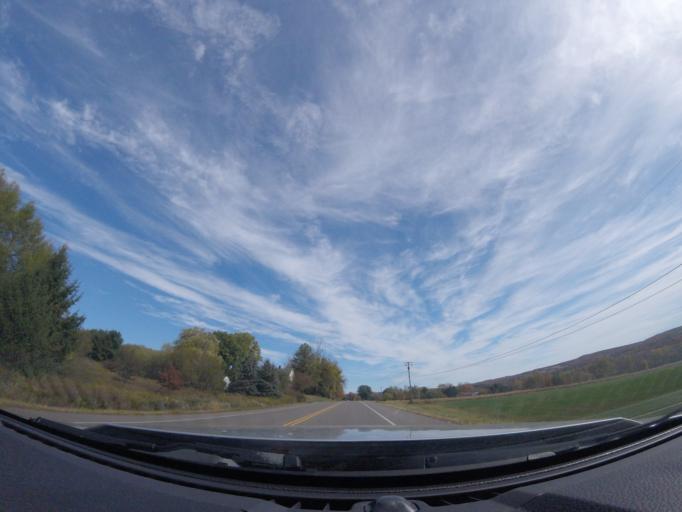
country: US
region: New York
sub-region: Cortland County
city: Cortland West
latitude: 42.5576
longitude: -76.2773
